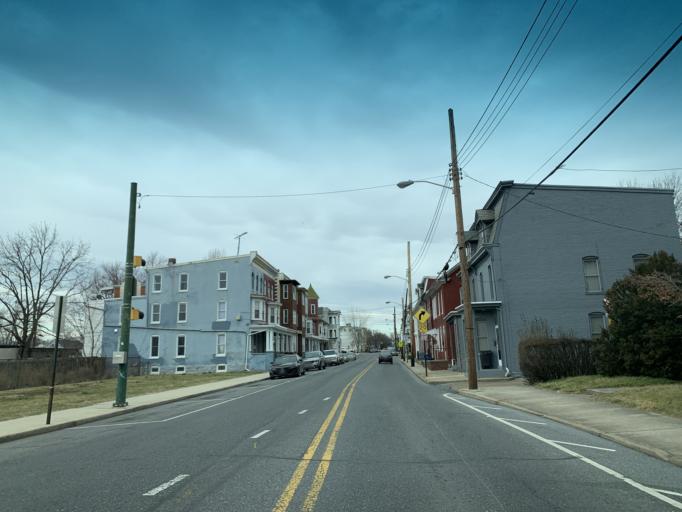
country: US
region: Maryland
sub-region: Washington County
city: Hagerstown
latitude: 39.6337
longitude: -77.7229
